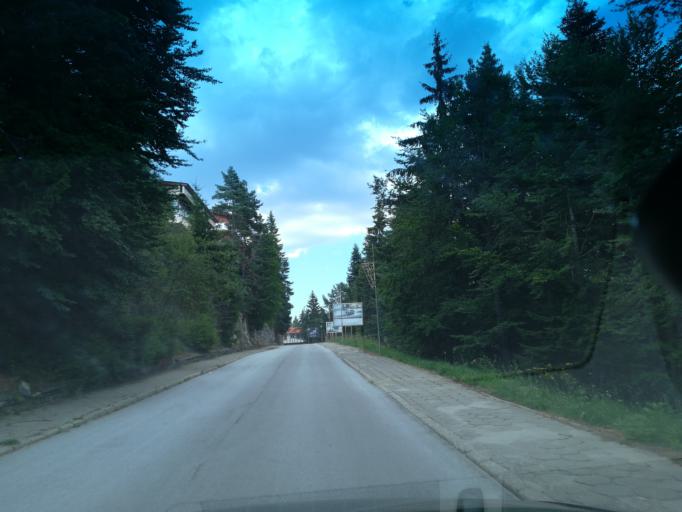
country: BG
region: Smolyan
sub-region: Obshtina Smolyan
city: Smolyan
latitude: 41.6552
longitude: 24.6944
